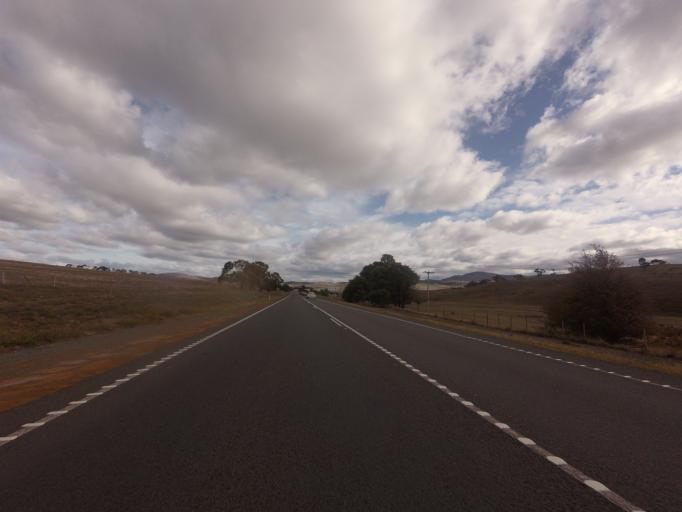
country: AU
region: Tasmania
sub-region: Brighton
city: Bridgewater
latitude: -42.4612
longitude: 147.1911
